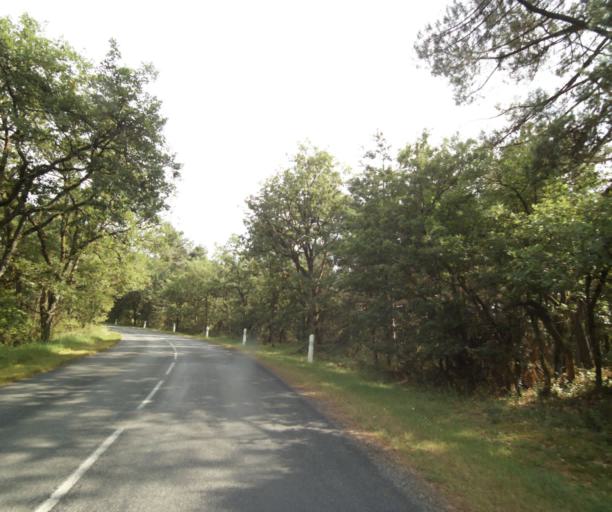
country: FR
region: Ile-de-France
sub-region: Departement de Seine-et-Marne
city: Acheres-la-Foret
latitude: 48.3714
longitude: 2.5606
